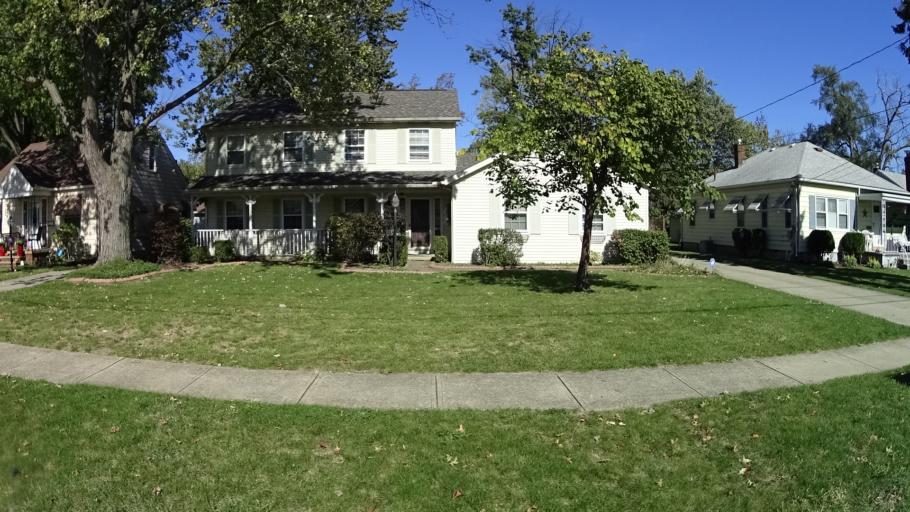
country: US
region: Ohio
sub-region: Lorain County
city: Lorain
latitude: 41.4438
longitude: -82.1801
